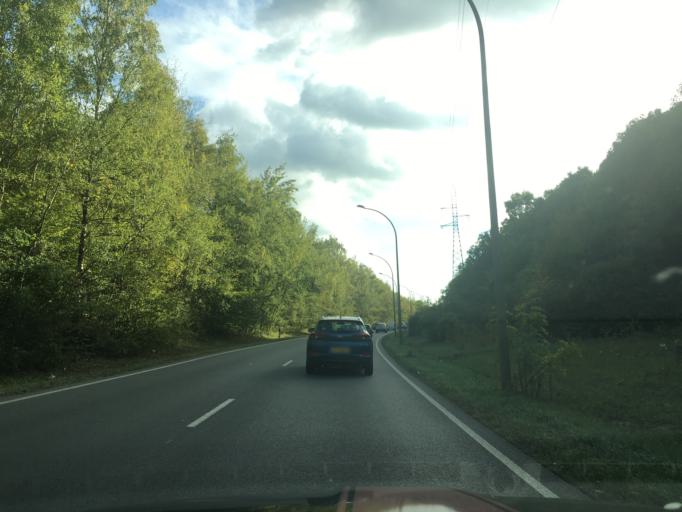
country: LU
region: Luxembourg
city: Soleuvre
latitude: 49.5291
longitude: 5.9269
